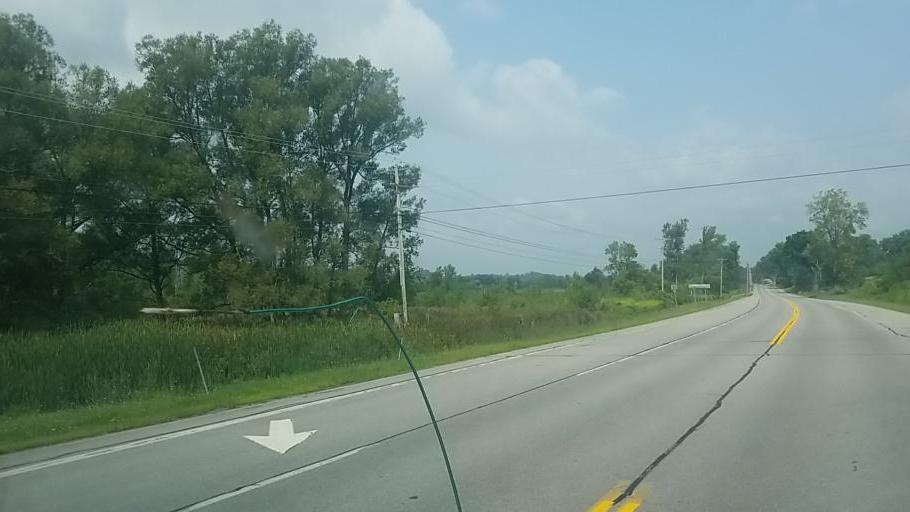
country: US
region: New York
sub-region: Montgomery County
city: Fort Plain
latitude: 42.9712
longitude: -74.6307
